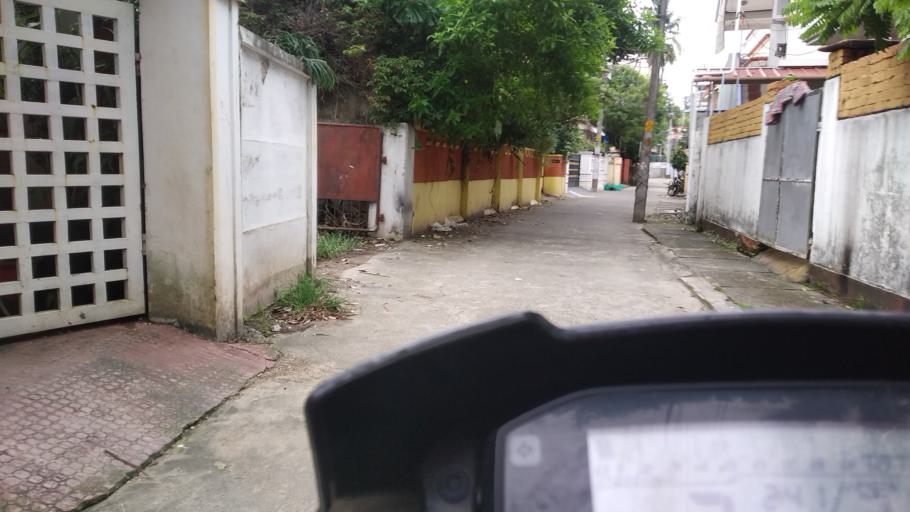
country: IN
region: Kerala
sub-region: Ernakulam
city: Cochin
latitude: 10.0001
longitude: 76.2808
